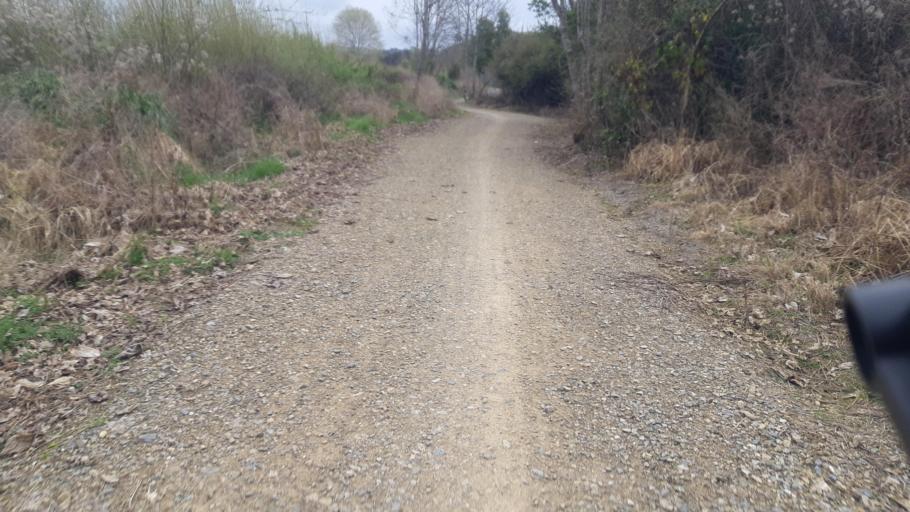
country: NZ
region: Tasman
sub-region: Tasman District
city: Wakefield
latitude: -41.4045
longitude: 173.0237
